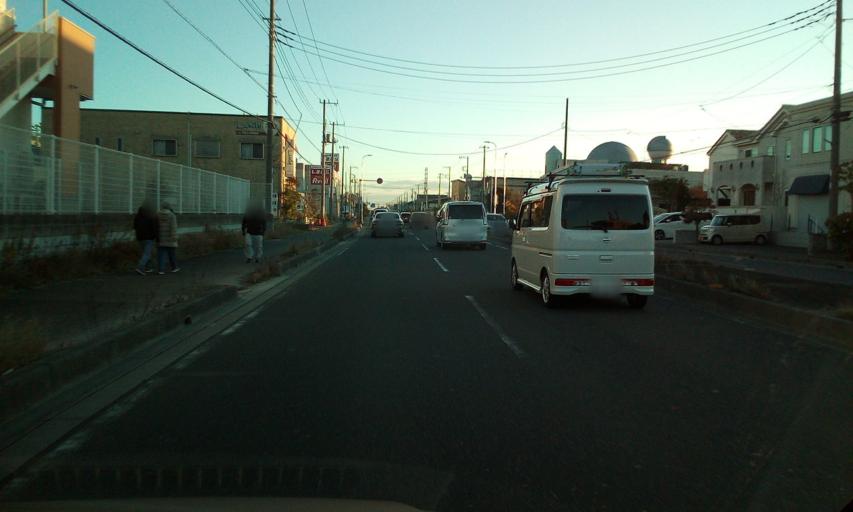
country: JP
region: Saitama
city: Yoshikawa
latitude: 35.8701
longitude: 139.8480
